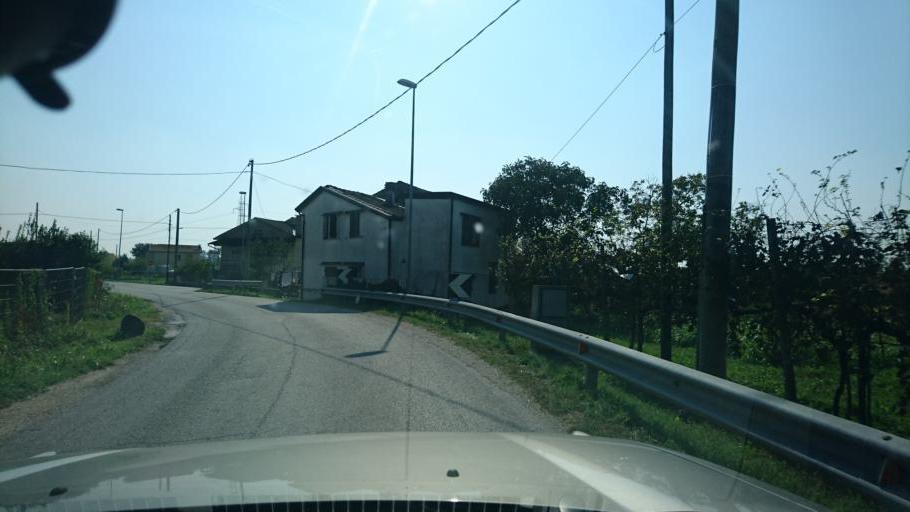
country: IT
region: Veneto
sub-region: Provincia di Padova
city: Gazzo
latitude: 45.5530
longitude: 11.7088
